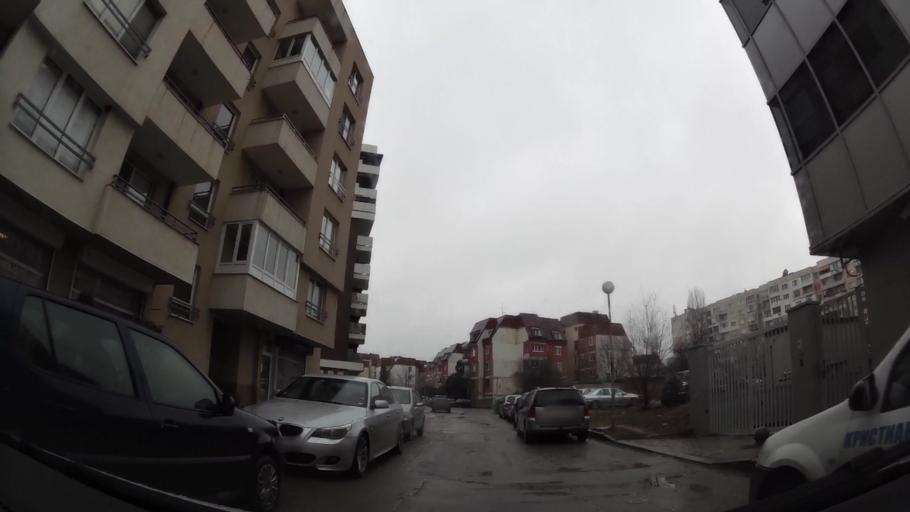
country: BG
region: Sofia-Capital
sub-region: Stolichna Obshtina
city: Sofia
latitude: 42.6267
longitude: 23.3804
